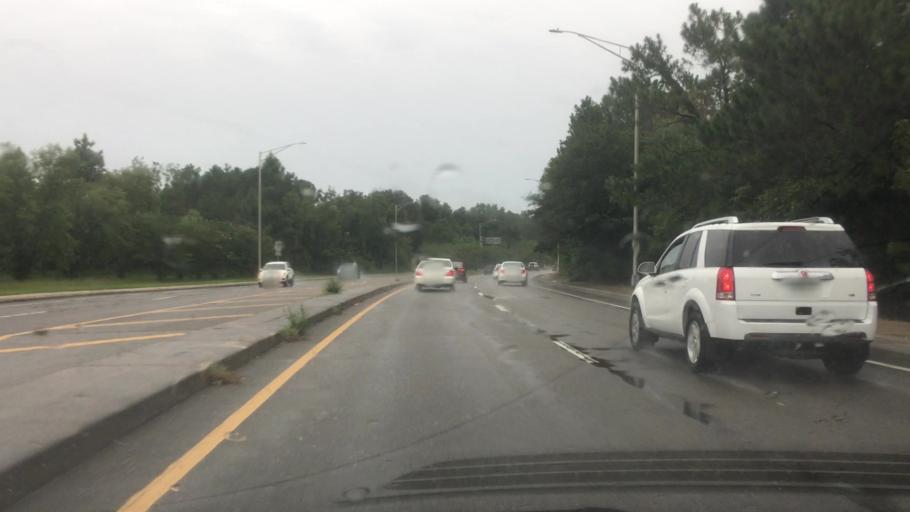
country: US
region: Florida
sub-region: Duval County
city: Jacksonville Beach
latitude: 30.2701
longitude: -81.5241
